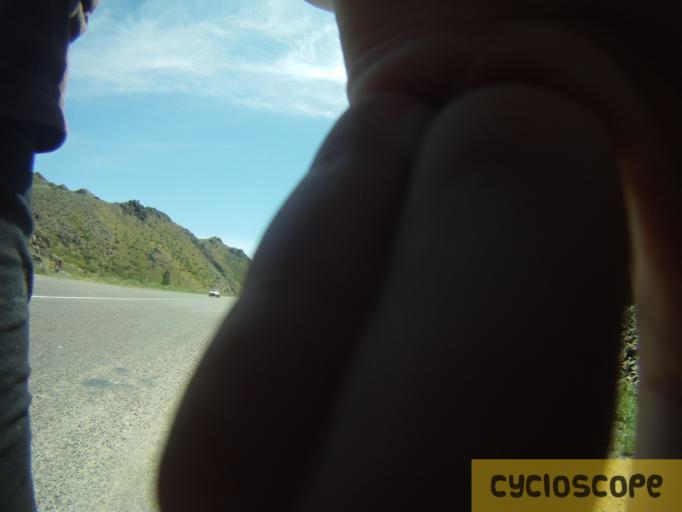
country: KZ
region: Almaty Oblysy
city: Kegen
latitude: 43.4657
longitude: 78.6416
